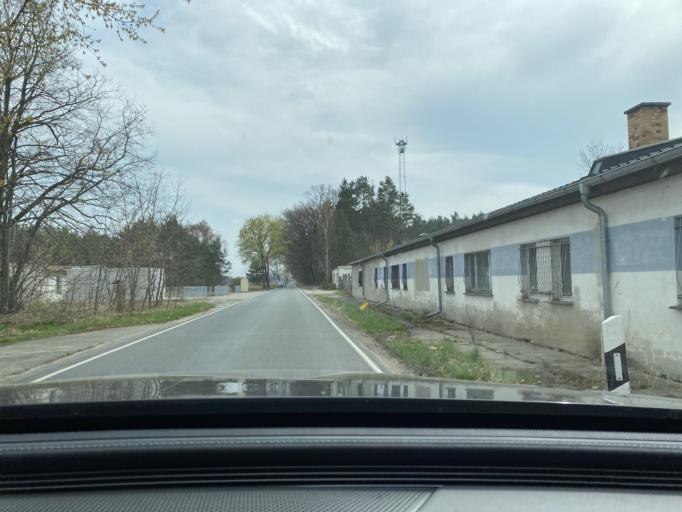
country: DE
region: Saxony
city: Konigswartha
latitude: 51.3088
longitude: 14.3123
